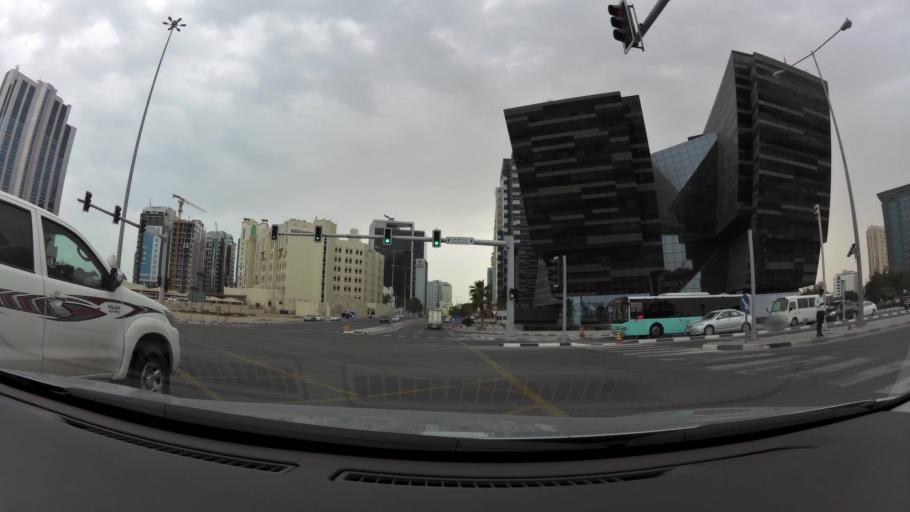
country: QA
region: Baladiyat ad Dawhah
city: Doha
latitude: 25.2918
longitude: 51.5440
